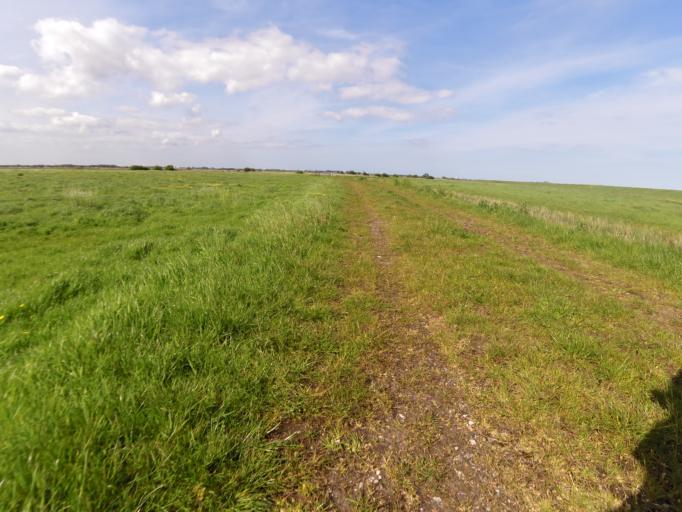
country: GB
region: England
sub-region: Norfolk
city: Great Yarmouth
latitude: 52.6140
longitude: 1.6890
